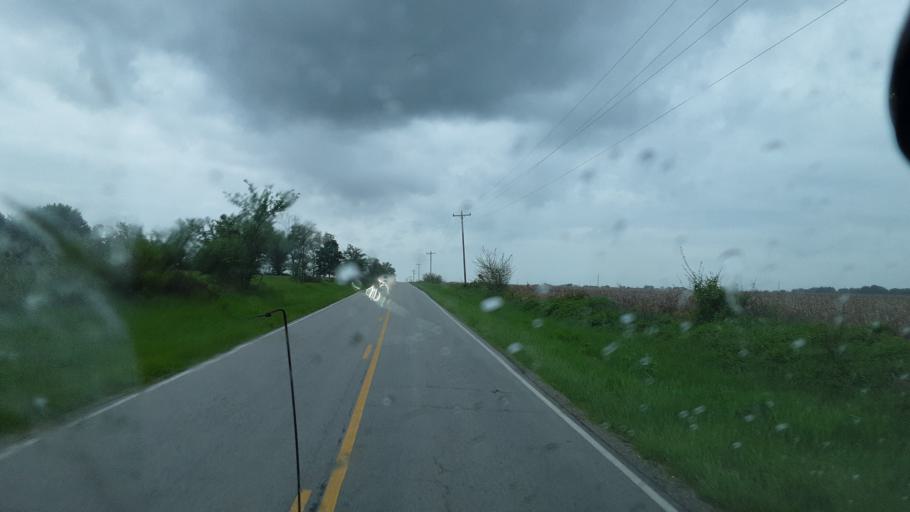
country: US
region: Missouri
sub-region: Boone County
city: Centralia
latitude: 39.4096
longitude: -92.2101
